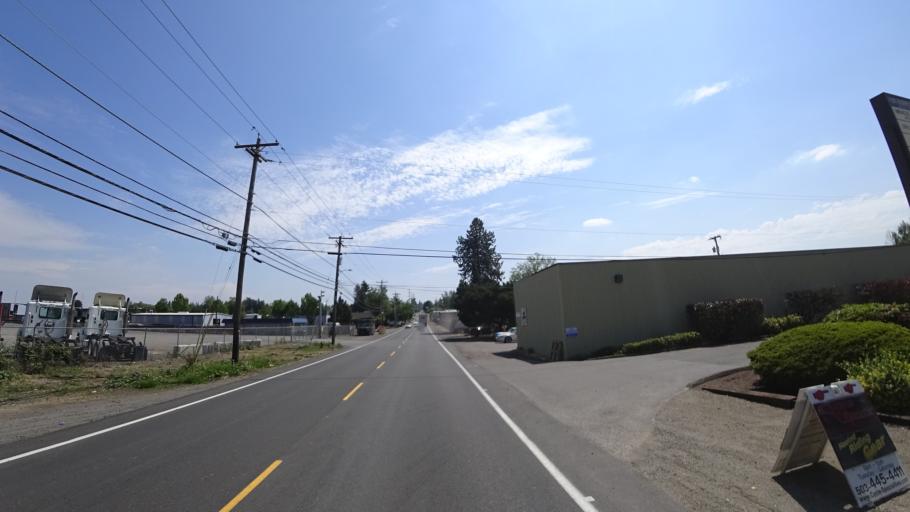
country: US
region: Oregon
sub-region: Multnomah County
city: Lents
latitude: 45.5641
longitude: -122.5548
